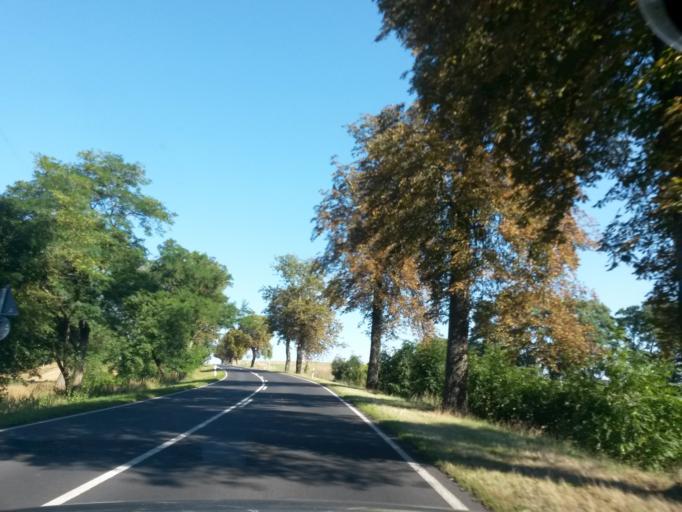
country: DE
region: Brandenburg
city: Angermunde
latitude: 53.0639
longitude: 13.9637
